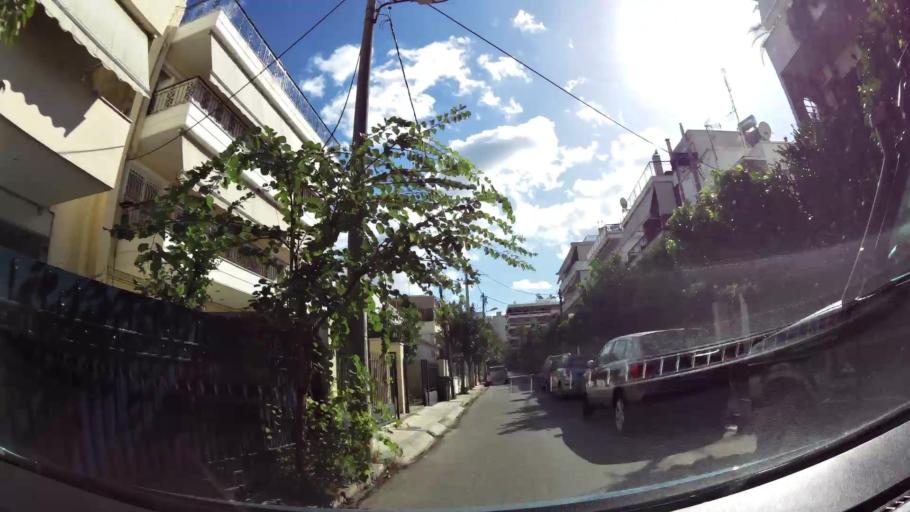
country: GR
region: Attica
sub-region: Nomarchia Athinas
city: Neo Psychiko
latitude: 38.0038
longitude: 23.7859
